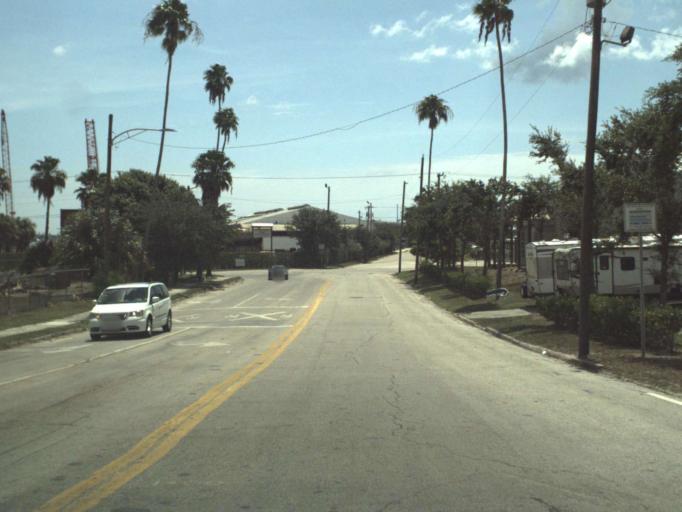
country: US
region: Florida
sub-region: Saint Lucie County
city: Fort Pierce
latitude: 27.4571
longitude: -80.3277
